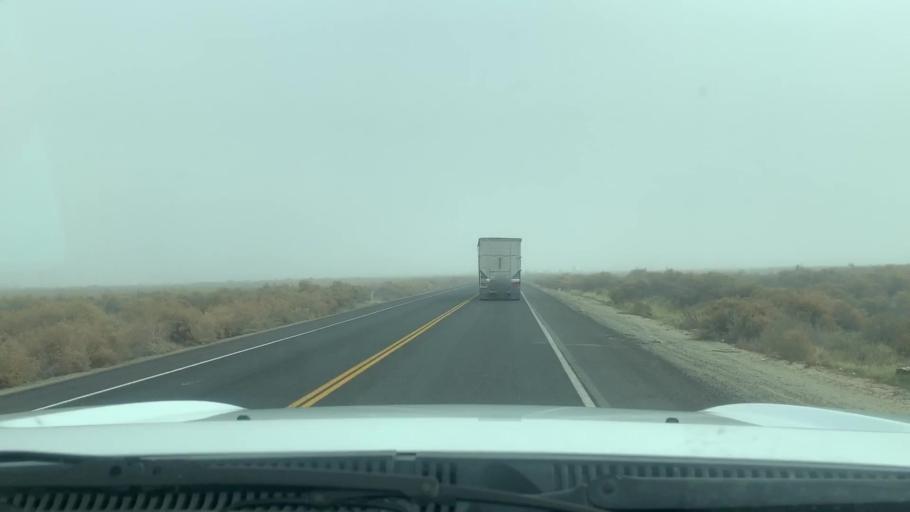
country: US
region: California
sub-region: Kern County
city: Buttonwillow
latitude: 35.4996
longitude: -119.5427
